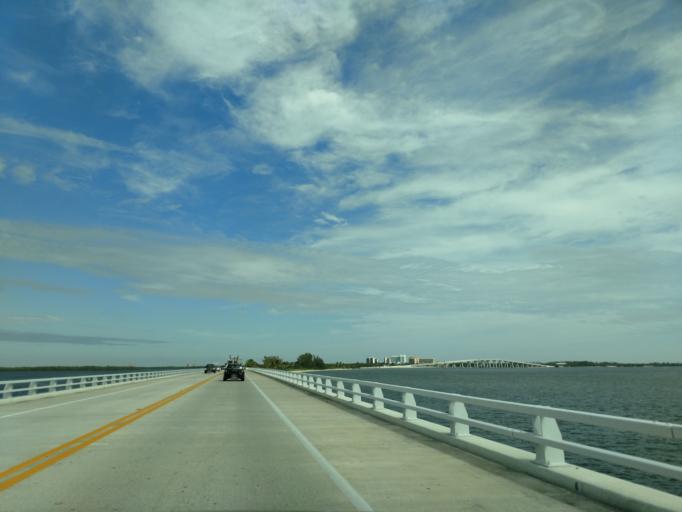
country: US
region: Florida
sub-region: Lee County
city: Punta Rassa
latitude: 26.4733
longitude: -82.0273
